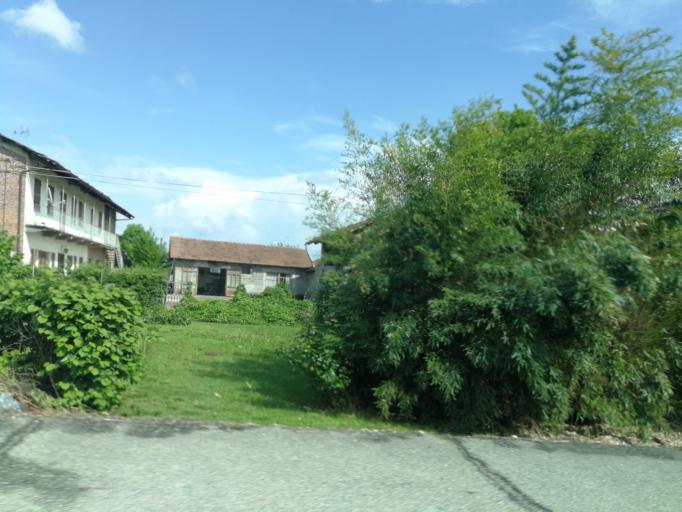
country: IT
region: Piedmont
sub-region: Provincia di Cuneo
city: Moretta
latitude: 44.7658
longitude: 7.5436
